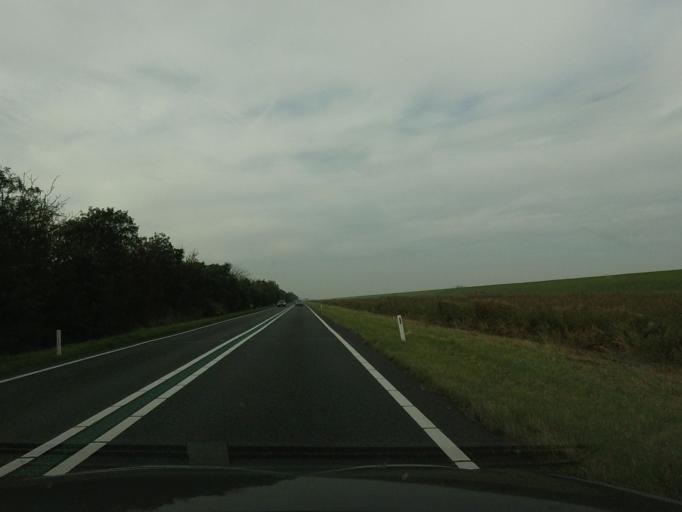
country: NL
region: North Holland
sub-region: Gemeente Den Helder
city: Den Helder
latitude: 52.8918
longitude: 4.8577
